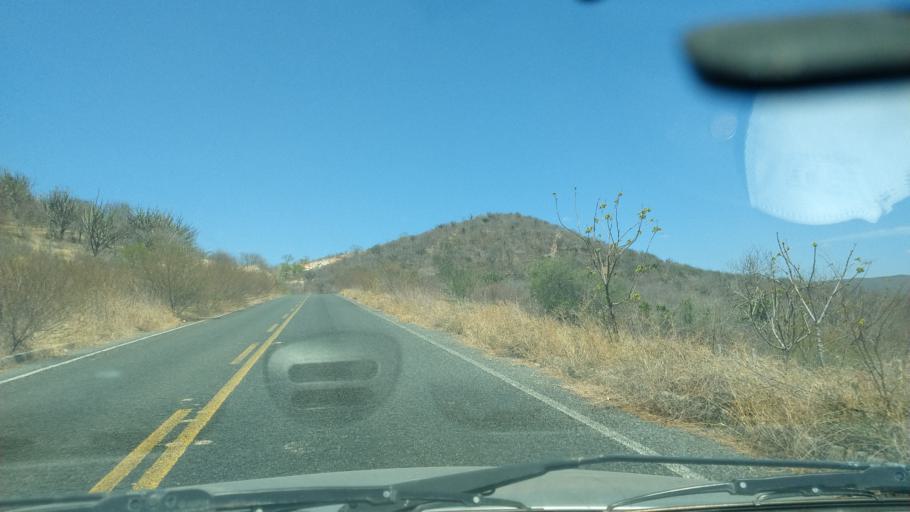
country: BR
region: Rio Grande do Norte
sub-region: Sao Tome
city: Sao Tome
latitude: -5.9689
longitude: -36.1552
